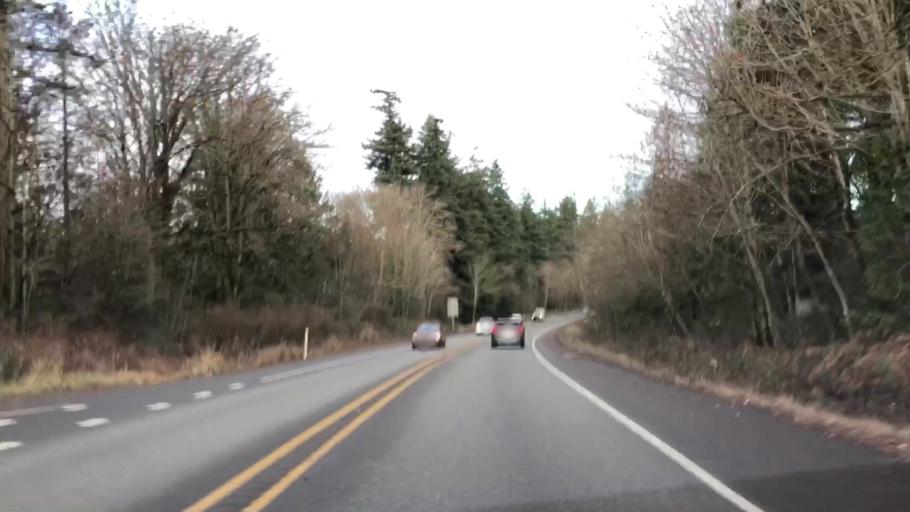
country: US
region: Washington
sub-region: Kitsap County
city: Bainbridge Island
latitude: 47.6459
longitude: -122.5214
